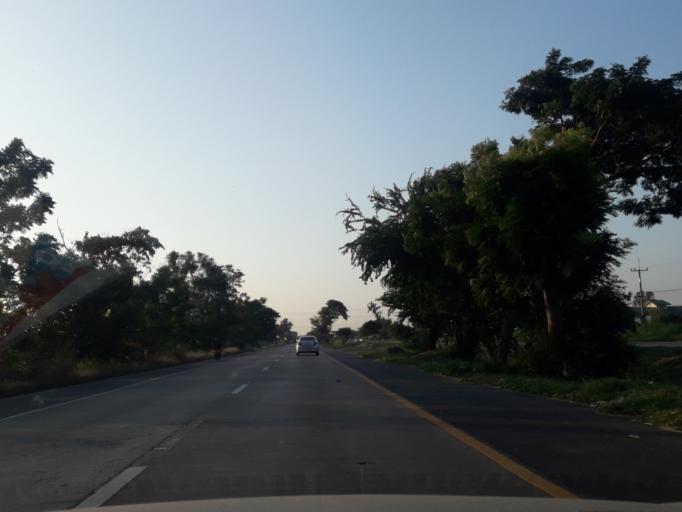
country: TH
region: Phra Nakhon Si Ayutthaya
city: Bang Pa-in
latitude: 14.2797
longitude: 100.5282
